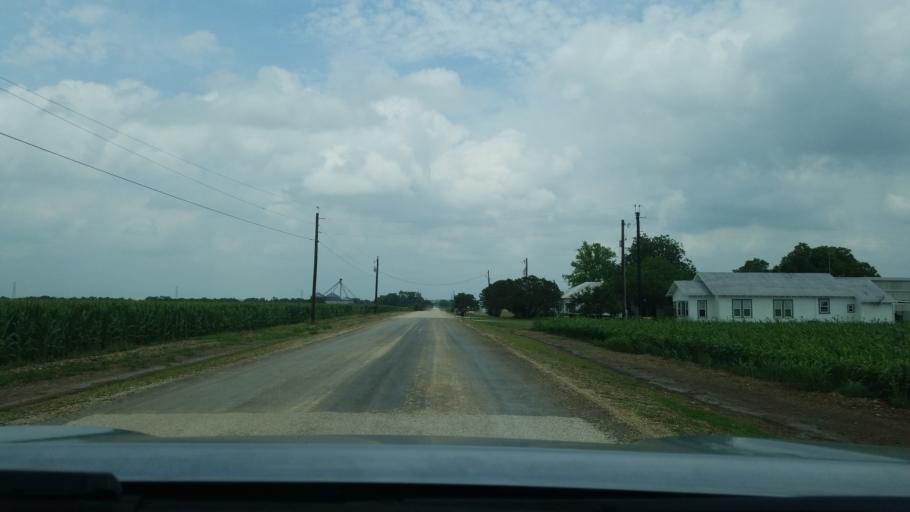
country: US
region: Texas
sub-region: Guadalupe County
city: Geronimo
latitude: 29.6814
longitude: -98.0031
